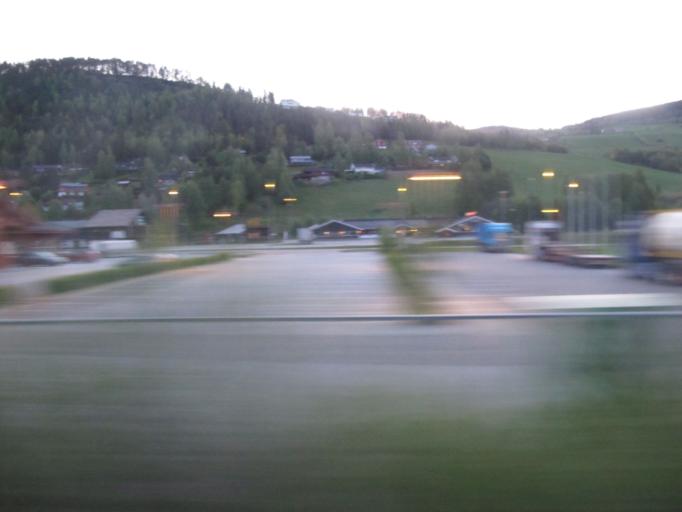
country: NO
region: Oppland
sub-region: Nord-Fron
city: Vinstra
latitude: 61.5886
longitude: 9.7675
